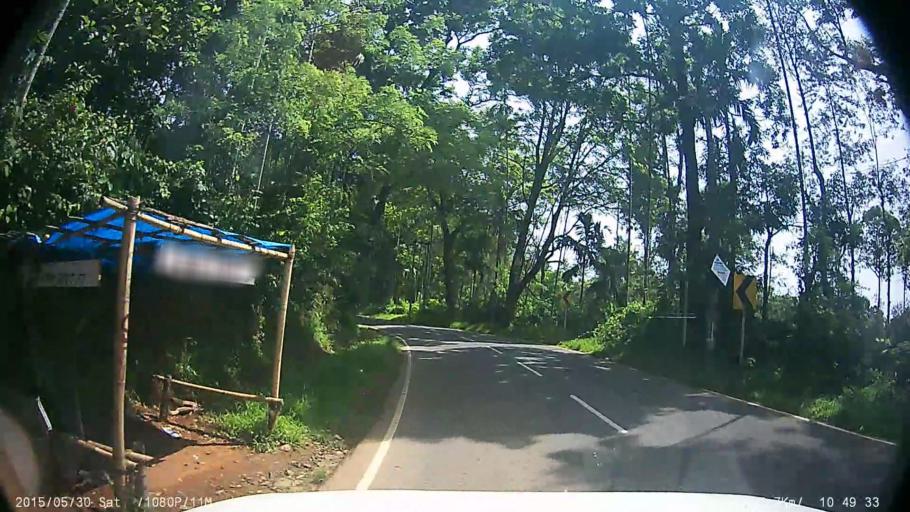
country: IN
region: Kerala
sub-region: Wayanad
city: Kalpetta
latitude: 11.6380
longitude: 76.0863
